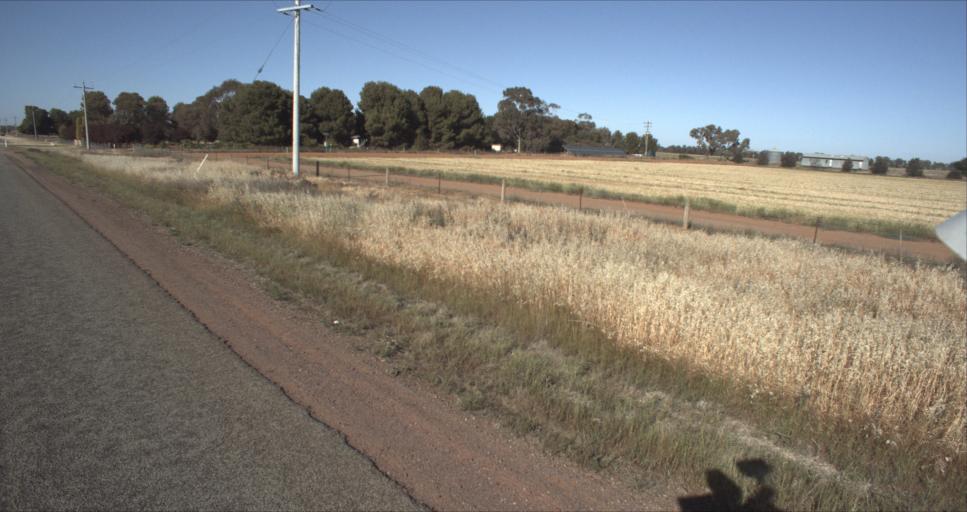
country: AU
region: New South Wales
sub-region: Leeton
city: Leeton
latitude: -34.5834
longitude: 146.2611
